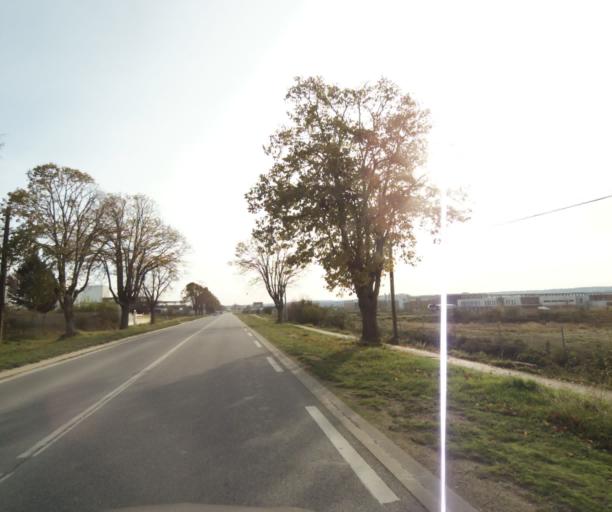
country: FR
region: Ile-de-France
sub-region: Departement des Yvelines
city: Triel-sur-Seine
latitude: 48.9577
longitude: 2.0184
